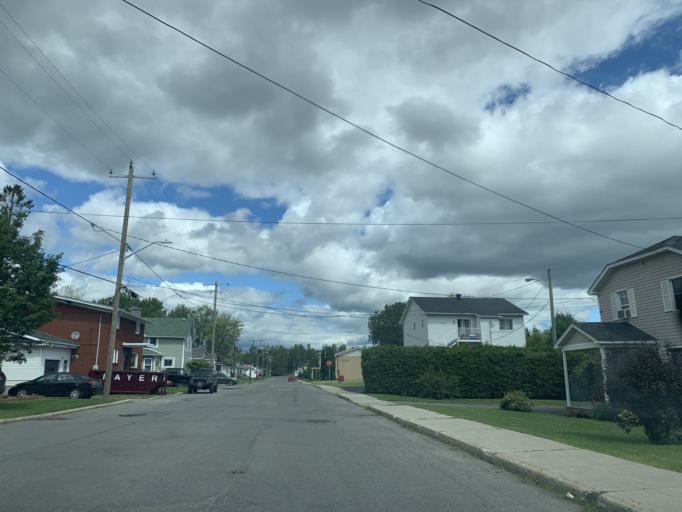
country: CA
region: Ontario
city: Hawkesbury
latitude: 45.6079
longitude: -74.6202
